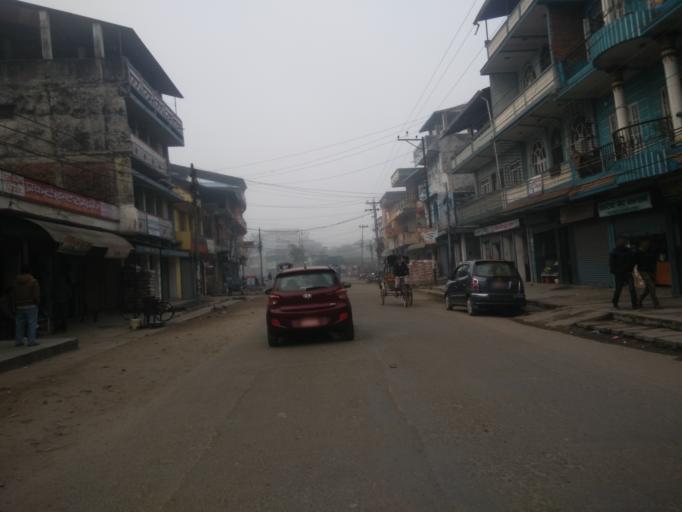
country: NP
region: Central Region
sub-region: Narayani Zone
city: Bharatpur
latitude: 27.6901
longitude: 84.4198
